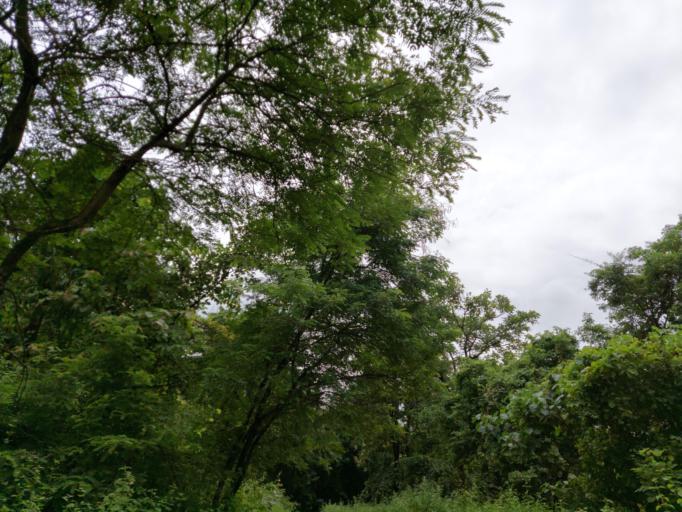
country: IN
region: Maharashtra
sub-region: Ratnagiri
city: Chiplun
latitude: 17.5580
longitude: 73.5073
